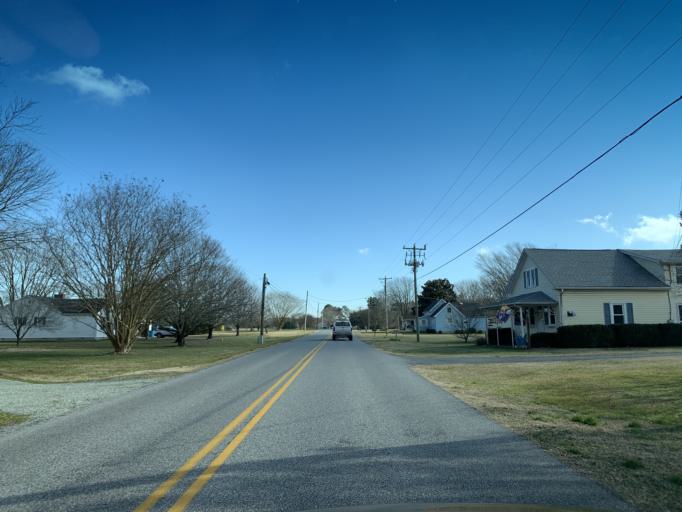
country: US
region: Maryland
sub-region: Worcester County
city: Ocean Pines
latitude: 38.4248
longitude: -75.1682
